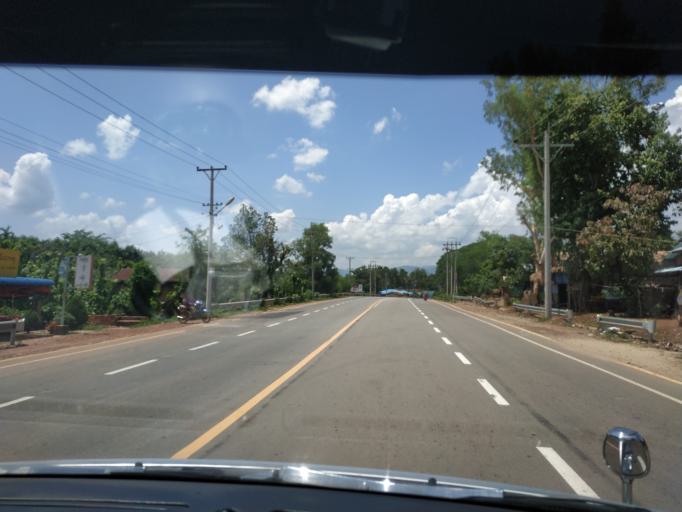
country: MM
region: Mon
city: Kyaikto
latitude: 17.3447
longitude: 97.0371
